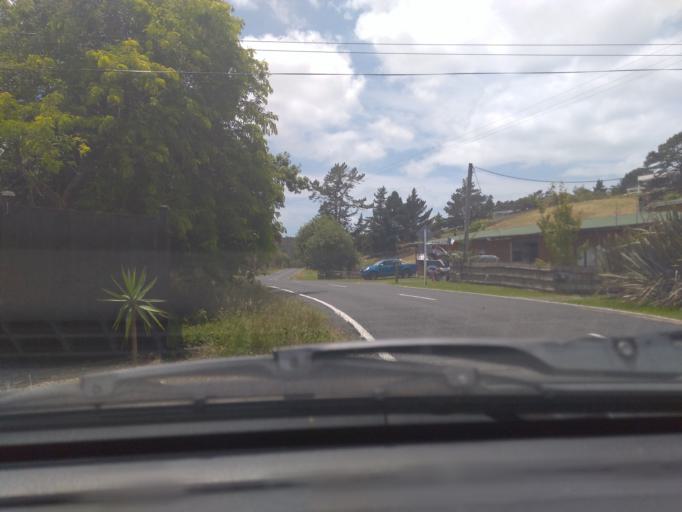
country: NZ
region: Auckland
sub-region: Auckland
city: Rothesay Bay
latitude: -36.6803
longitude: 174.6979
